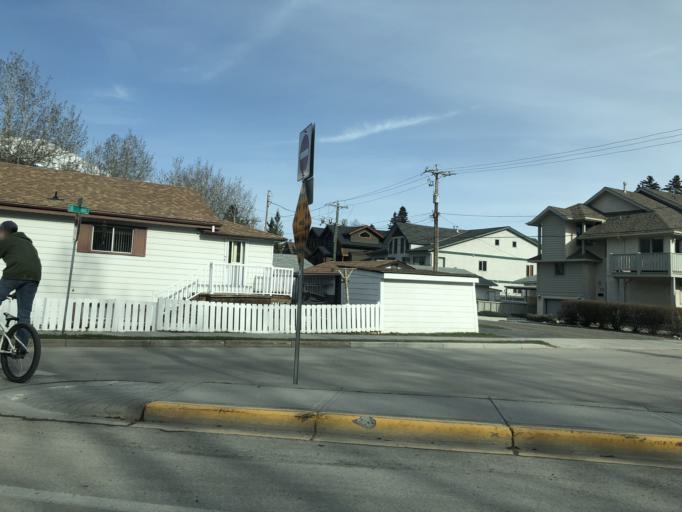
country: CA
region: Alberta
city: Canmore
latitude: 51.0870
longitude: -115.3634
